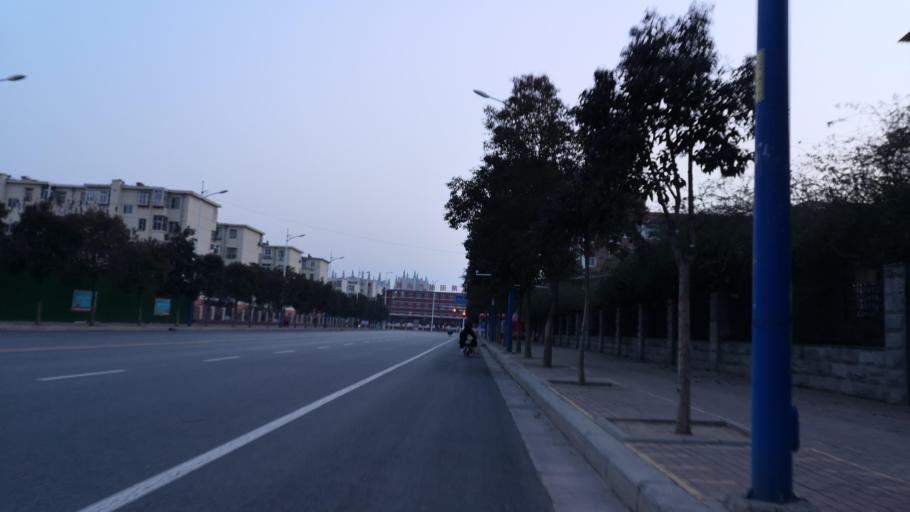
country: CN
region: Henan Sheng
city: Zhongyuanlu
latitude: 35.7650
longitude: 115.0627
